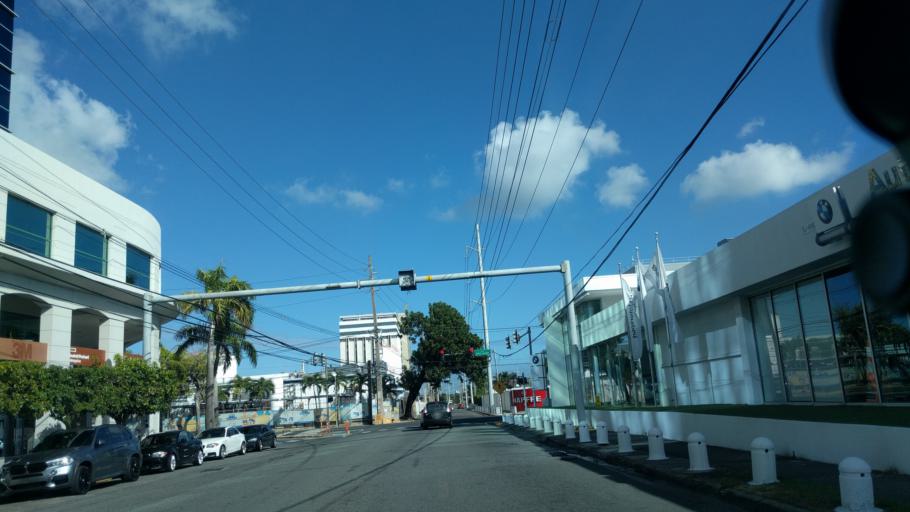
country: PR
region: Catano
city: Catano
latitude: 18.4232
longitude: -66.0676
